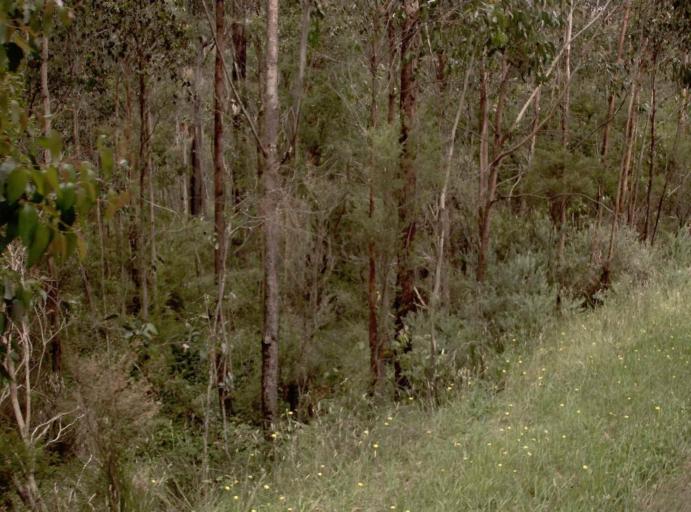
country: AU
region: Victoria
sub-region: Latrobe
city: Traralgon
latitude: -38.0154
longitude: 146.4208
